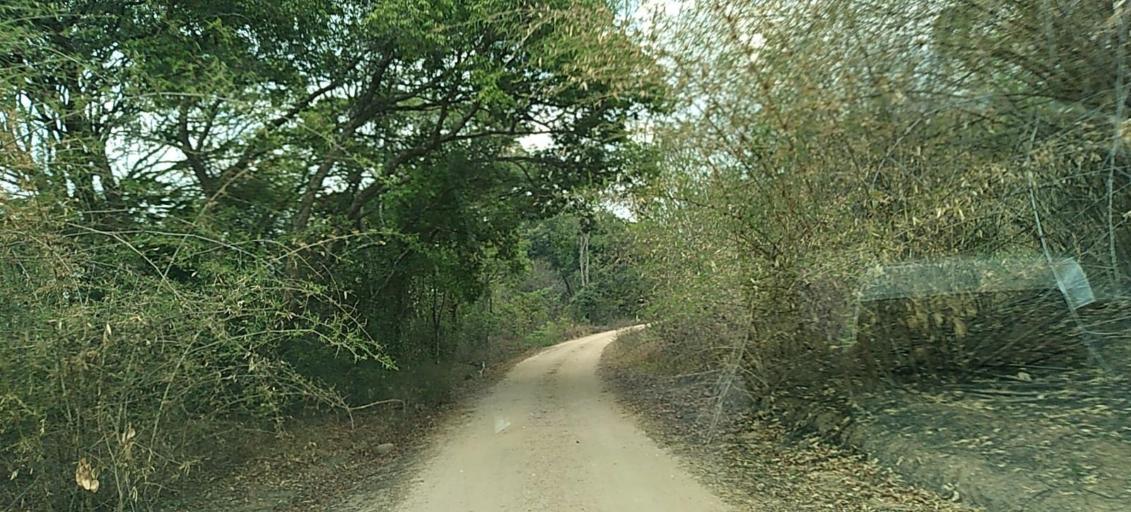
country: ZM
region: Copperbelt
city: Chingola
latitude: -12.7542
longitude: 27.7157
